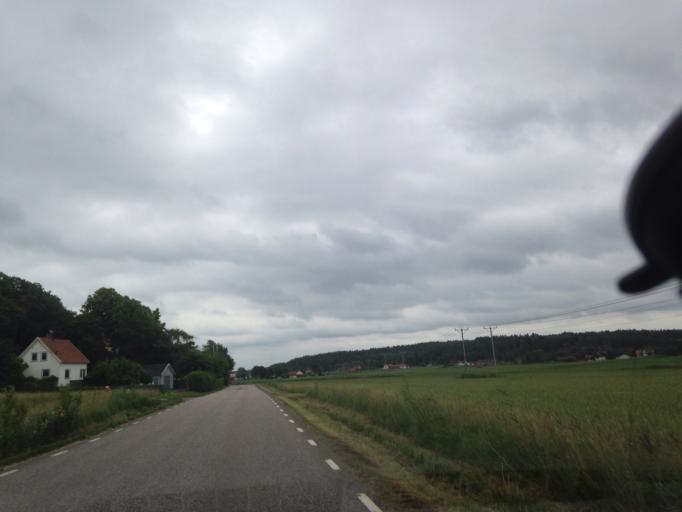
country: SE
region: Vaestra Goetaland
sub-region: Kungalvs Kommun
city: Kode
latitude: 57.8356
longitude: 11.7977
